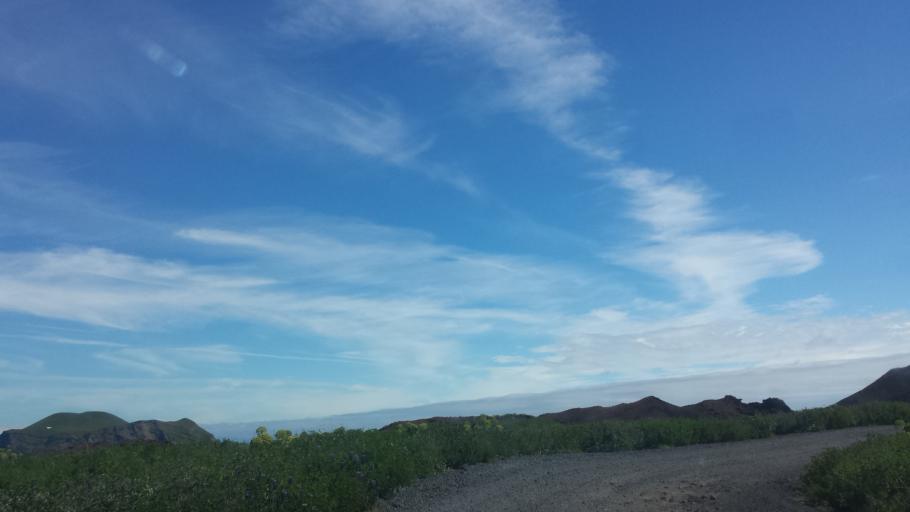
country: IS
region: South
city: Vestmannaeyjar
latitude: 63.4424
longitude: -20.2464
